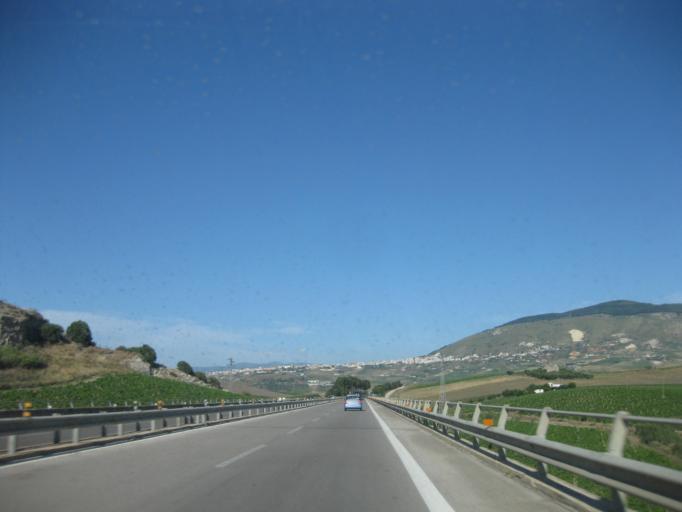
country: IT
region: Sicily
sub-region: Trapani
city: Castellammare del Golfo
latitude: 37.9684
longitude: 12.8942
